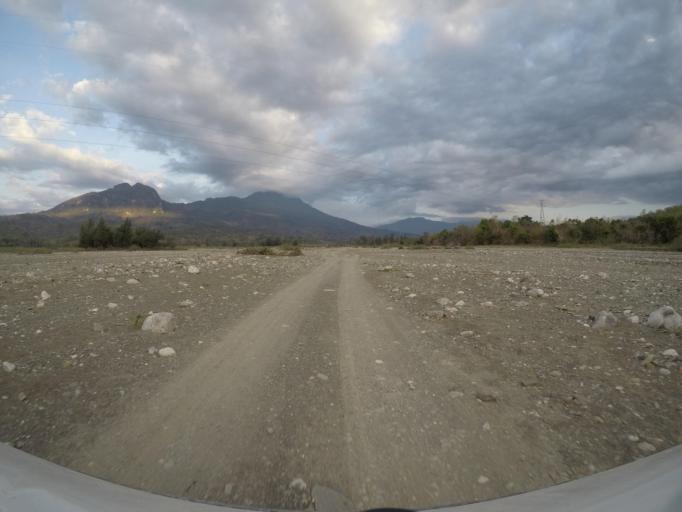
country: TL
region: Bobonaro
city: Maliana
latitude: -8.9073
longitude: 125.2113
